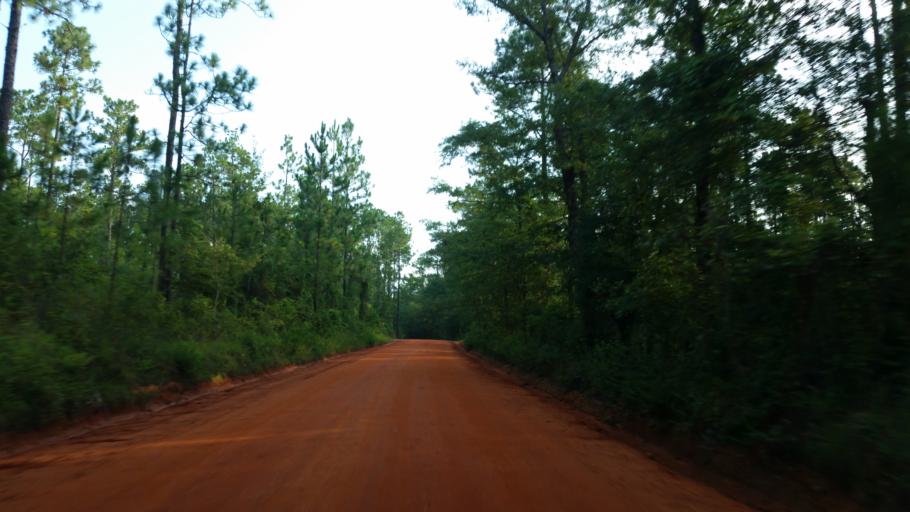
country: US
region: Alabama
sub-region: Escambia County
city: Atmore
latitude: 30.9210
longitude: -87.5761
